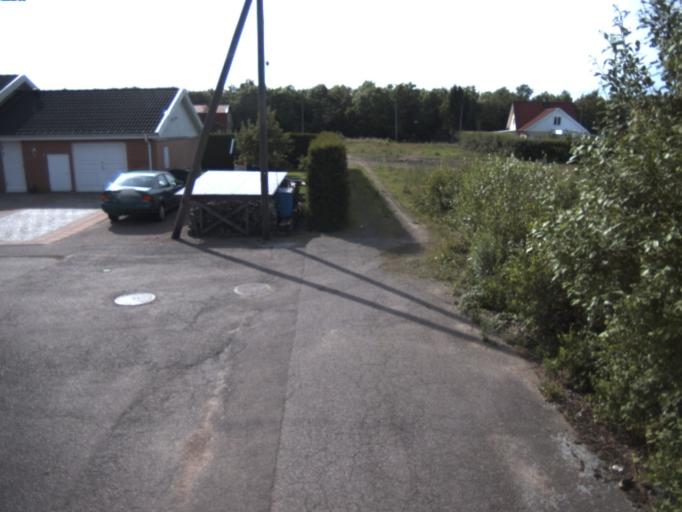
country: SE
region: Skane
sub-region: Helsingborg
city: Odakra
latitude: 56.0847
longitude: 12.7502
